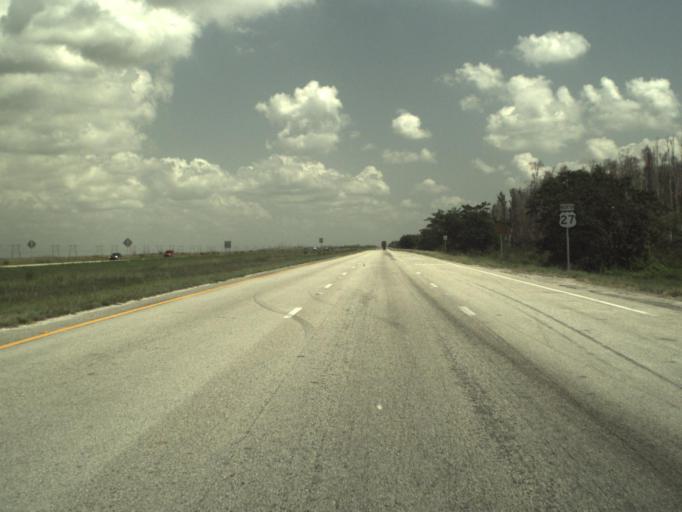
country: US
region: Florida
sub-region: Miami-Dade County
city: Palm Springs North
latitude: 25.9571
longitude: -80.4309
